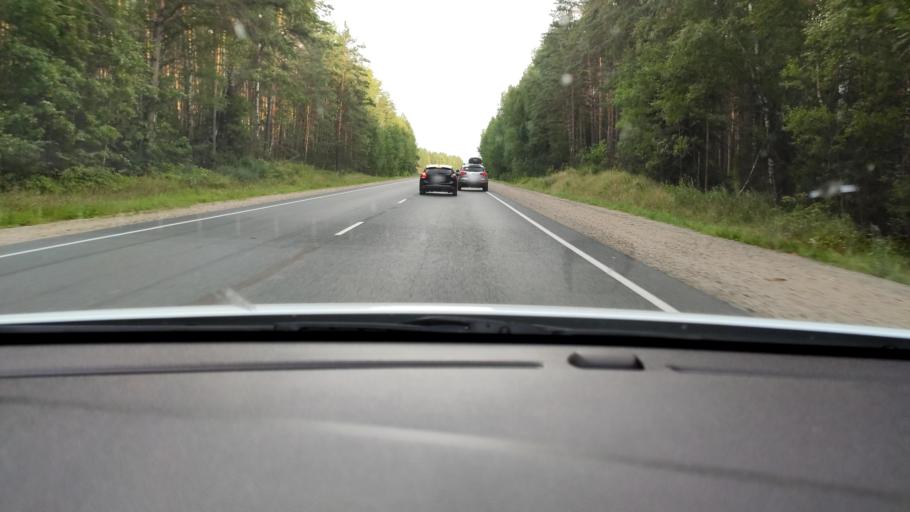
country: RU
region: Mariy-El
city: Pomary
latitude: 56.0051
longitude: 48.3803
